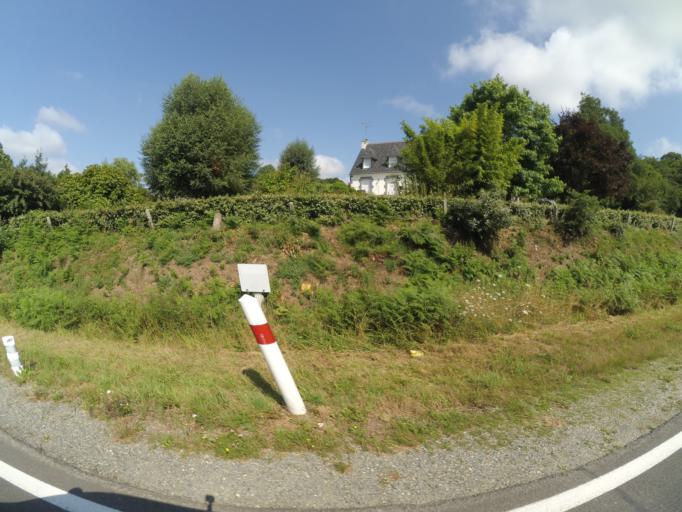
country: FR
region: Brittany
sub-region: Departement du Finistere
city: Bannalec
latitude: 47.9367
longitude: -3.7242
